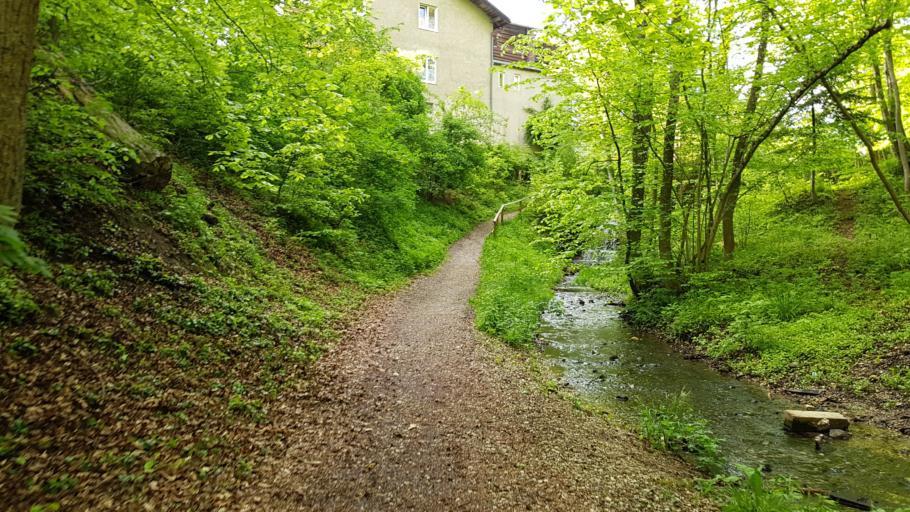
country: DE
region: Bavaria
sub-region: Upper Bavaria
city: Bad Endorf
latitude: 47.9118
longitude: 12.3026
